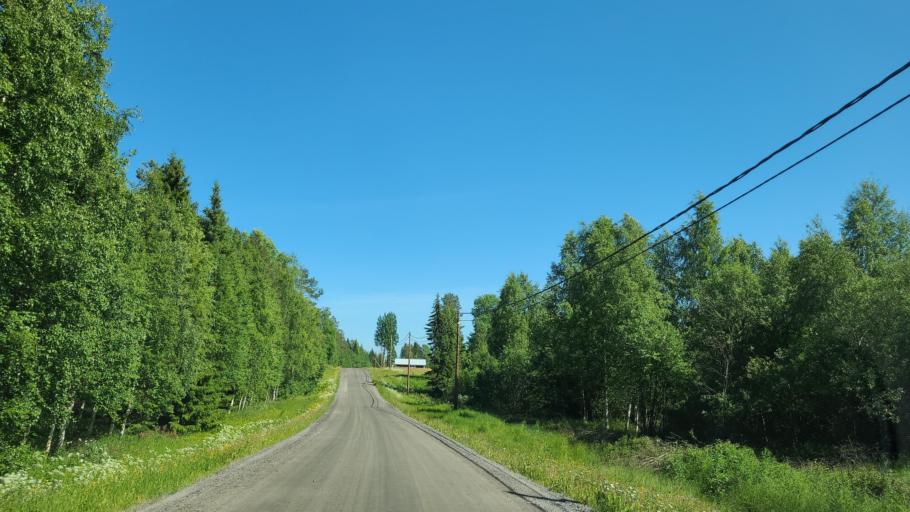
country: SE
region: Vaesterbotten
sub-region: Bjurholms Kommun
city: Bjurholm
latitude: 63.6398
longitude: 19.1830
